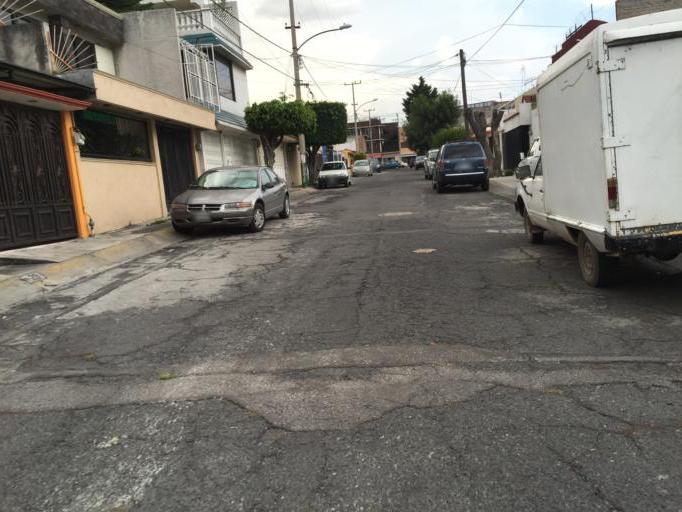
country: MX
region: Mexico
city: Cuautitlan Izcalli
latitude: 19.6530
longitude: -99.2146
